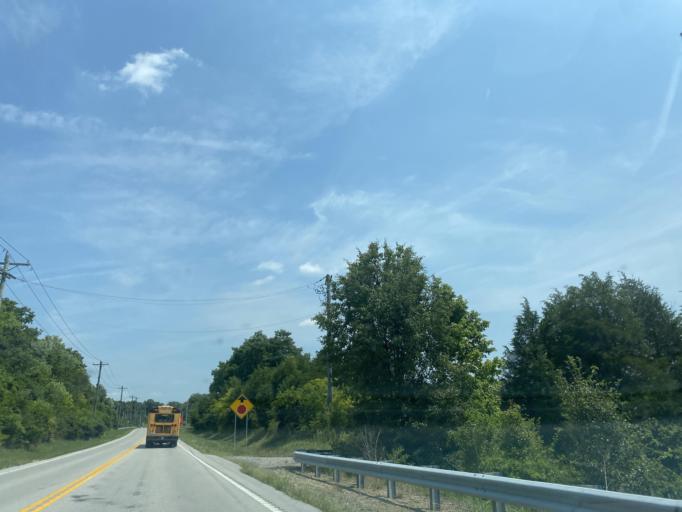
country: US
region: Kentucky
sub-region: Campbell County
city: Claryville
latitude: 38.9365
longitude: -84.4127
